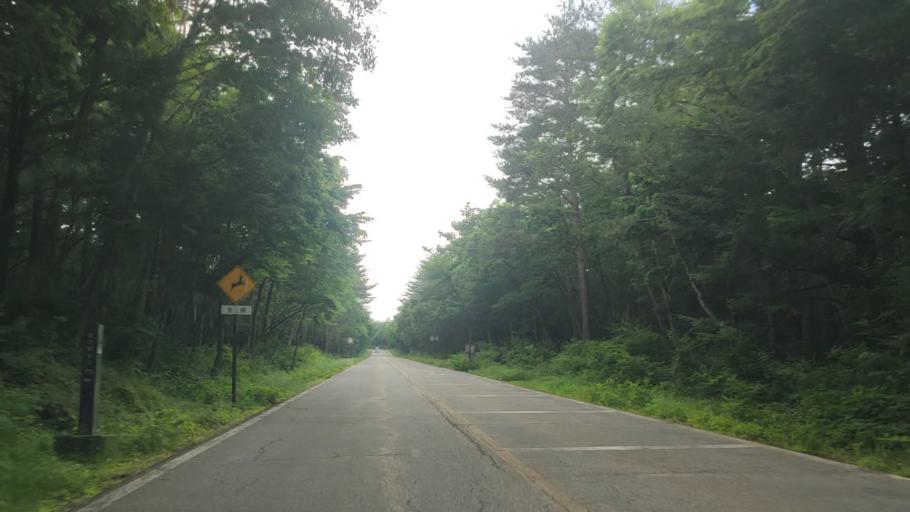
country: JP
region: Yamanashi
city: Fujikawaguchiko
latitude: 35.4444
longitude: 138.7521
